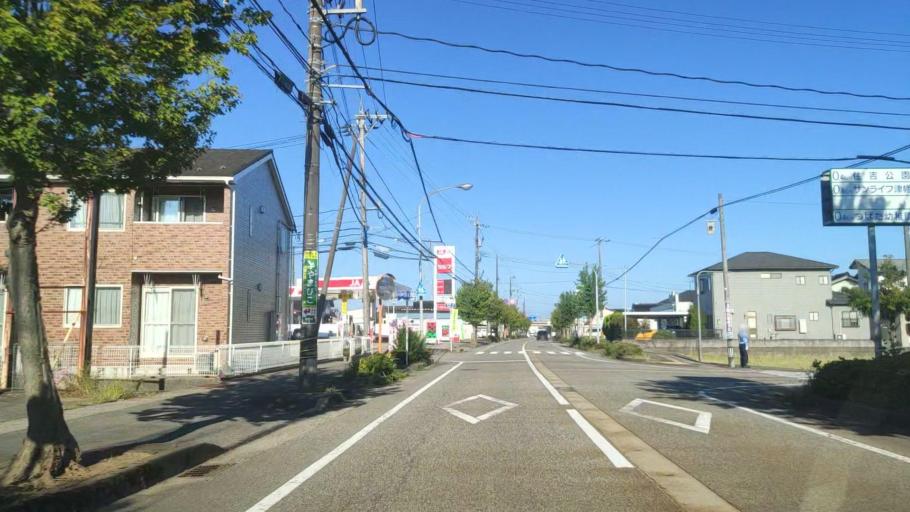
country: JP
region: Ishikawa
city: Tsubata
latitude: 36.6709
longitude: 136.7275
